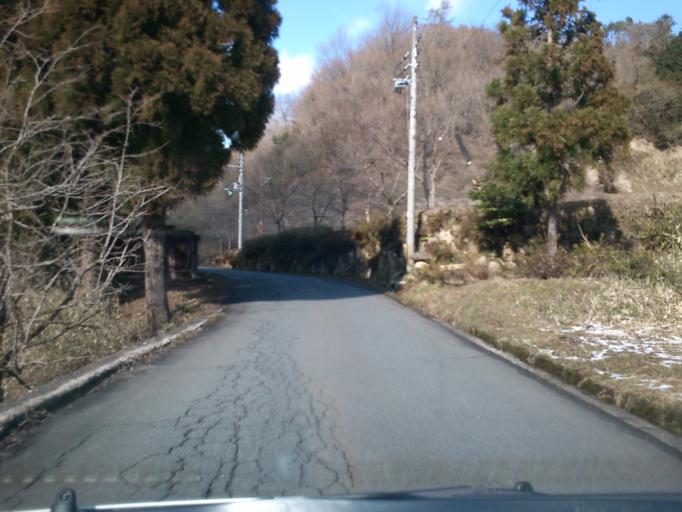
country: JP
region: Kyoto
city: Miyazu
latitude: 35.5858
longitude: 135.1779
